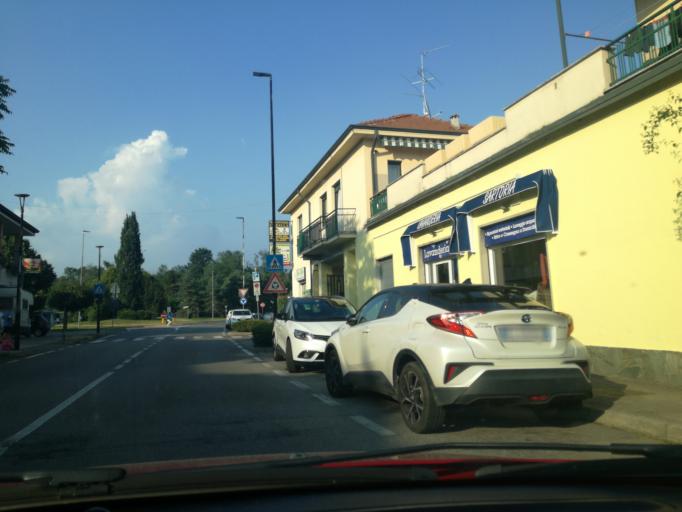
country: IT
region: Lombardy
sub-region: Provincia di Monza e Brianza
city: Usmate-Velate
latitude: 45.6530
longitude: 9.3659
